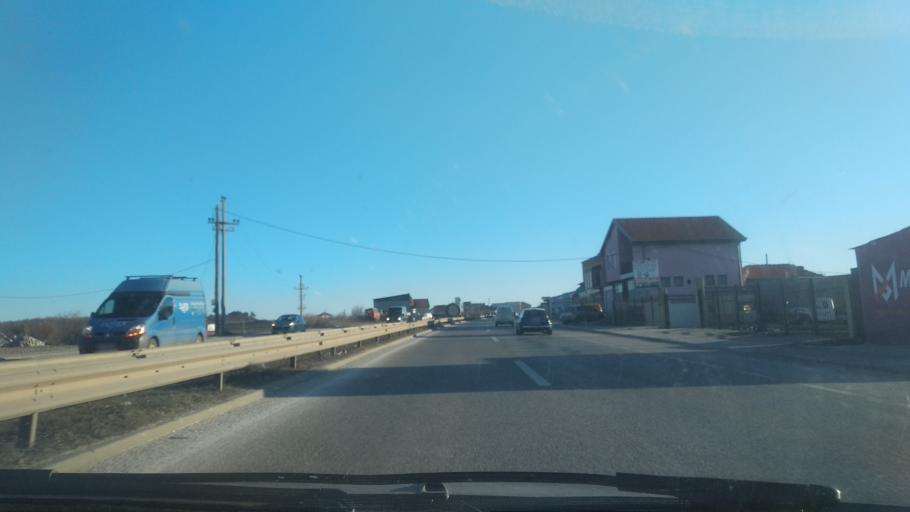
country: XK
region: Pristina
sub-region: Kosovo Polje
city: Kosovo Polje
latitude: 42.6950
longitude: 21.1160
